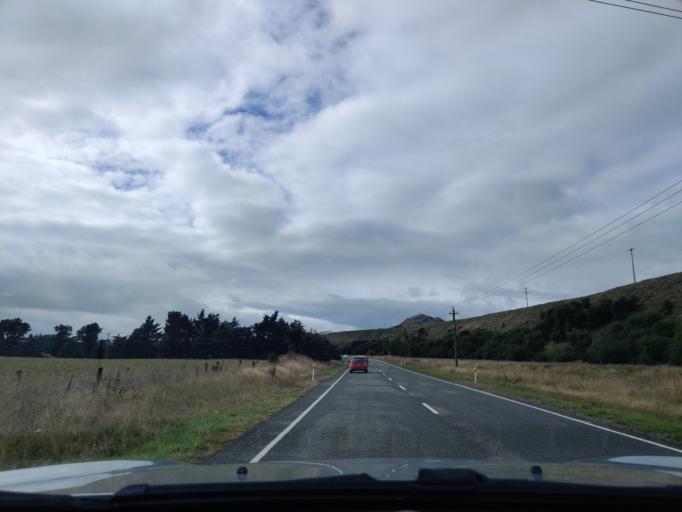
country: NZ
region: Canterbury
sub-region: Hurunui District
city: Amberley
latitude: -42.6990
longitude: 172.8051
